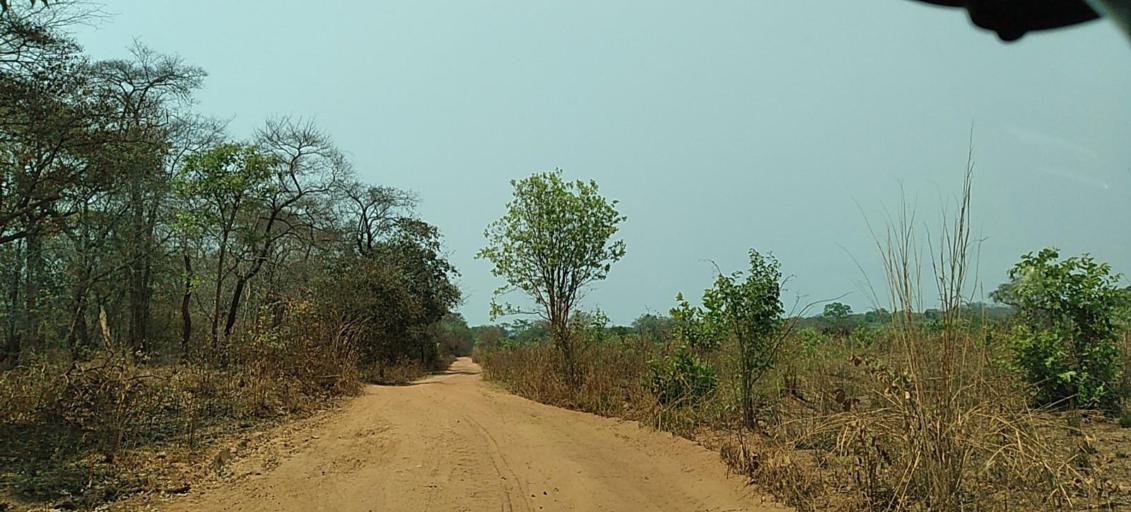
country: ZM
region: North-Western
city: Kabompo
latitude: -13.7033
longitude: 24.3201
